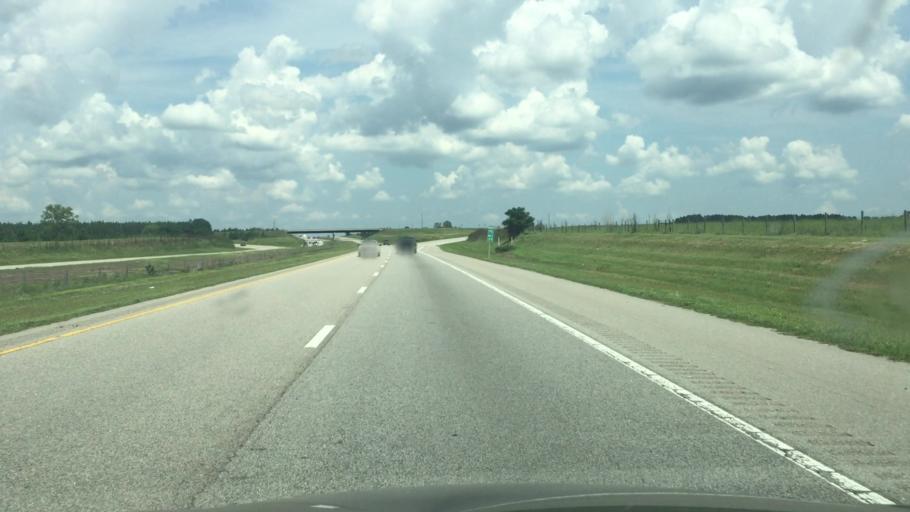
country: US
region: North Carolina
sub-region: Richmond County
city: Ellerbe
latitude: 35.1408
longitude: -79.7137
